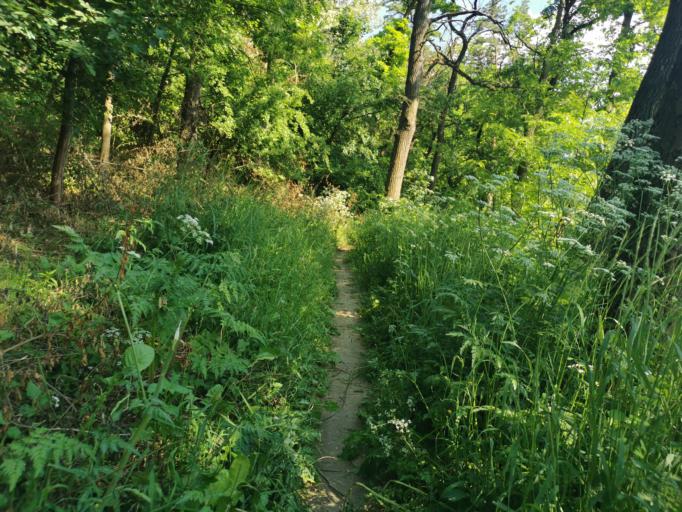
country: CZ
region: South Moravian
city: Knezdub
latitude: 48.8567
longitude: 17.3503
